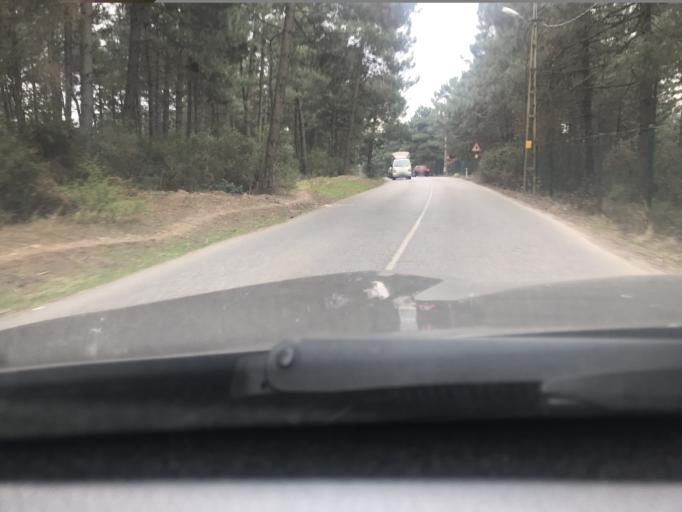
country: TR
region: Istanbul
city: Umraniye
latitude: 41.0485
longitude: 29.1702
